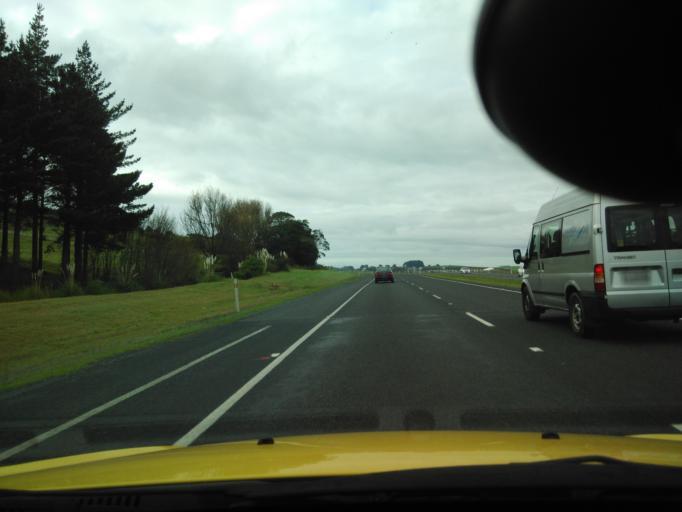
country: NZ
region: Waikato
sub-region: Waikato District
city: Te Kauwhata
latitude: -37.3433
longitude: 175.0674
